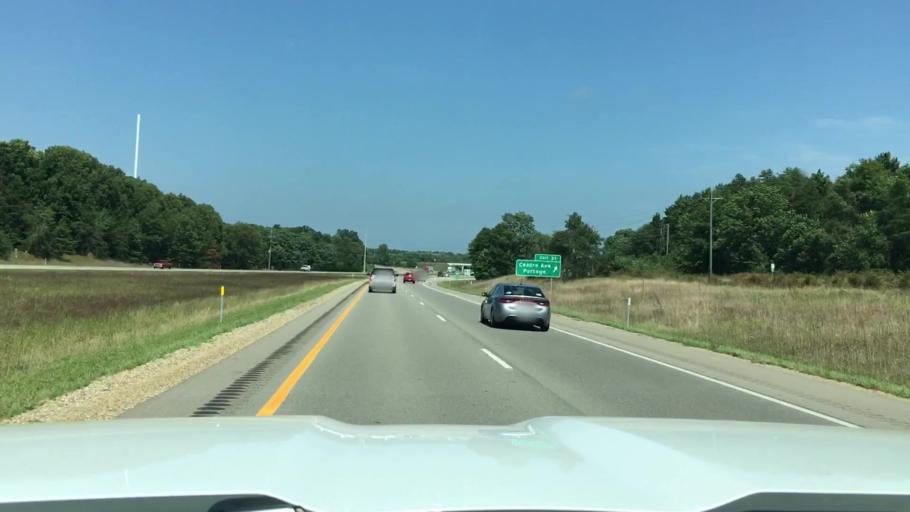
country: US
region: Michigan
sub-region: Kalamazoo County
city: Portage
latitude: 42.1928
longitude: -85.6463
